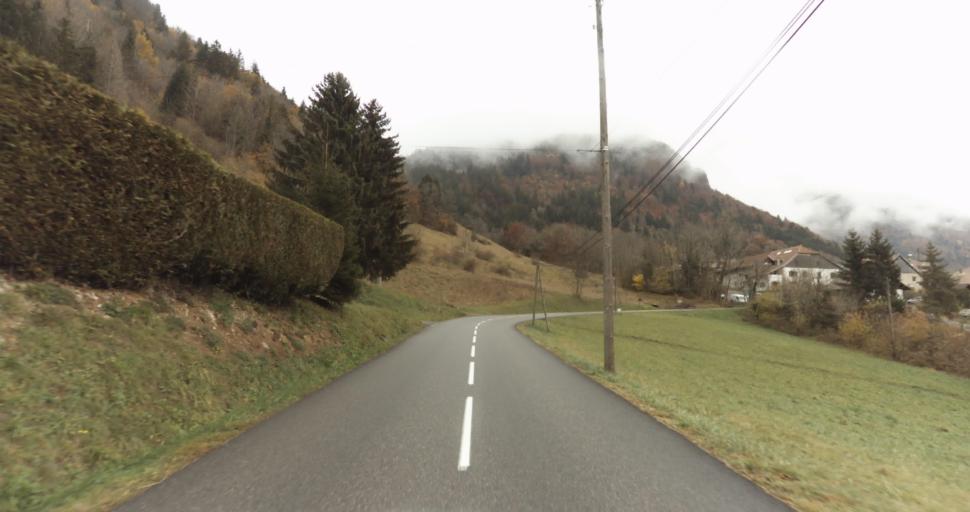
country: FR
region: Rhone-Alpes
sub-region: Departement de la Haute-Savoie
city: Thorens-Glieres
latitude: 45.9859
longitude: 6.2774
